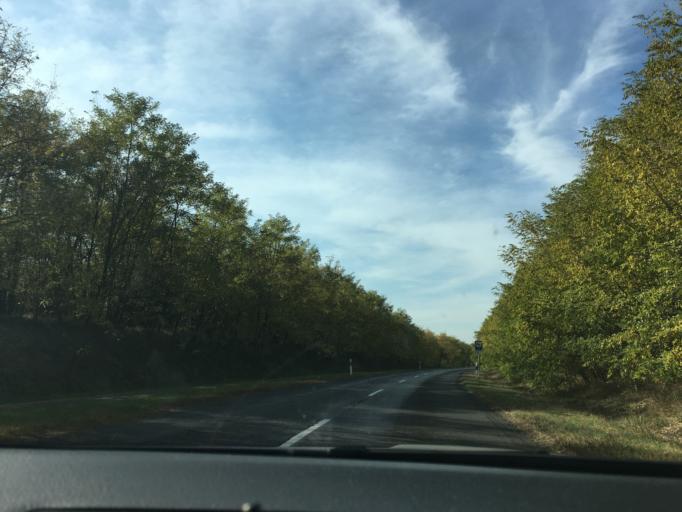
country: HU
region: Hajdu-Bihar
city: Vamospercs
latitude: 47.5255
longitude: 21.9452
